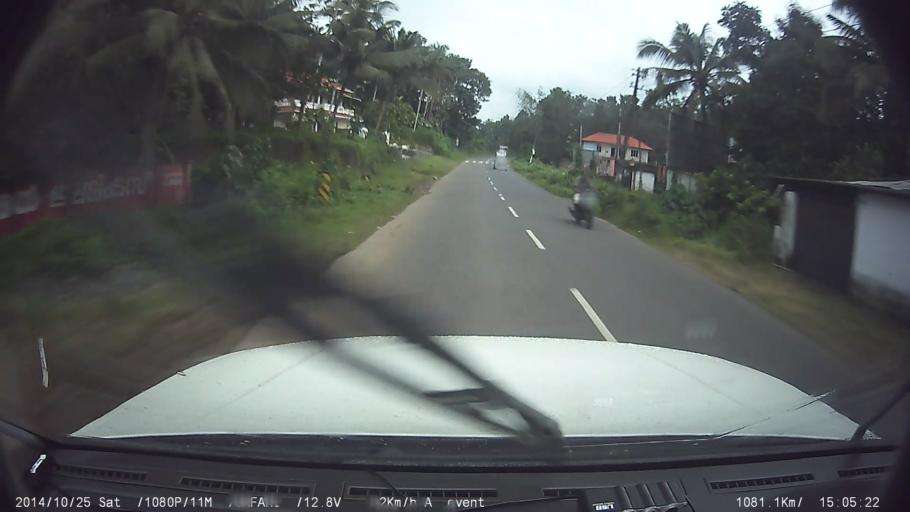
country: IN
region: Kerala
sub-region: Ernakulam
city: Piravam
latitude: 9.8374
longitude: 76.5918
